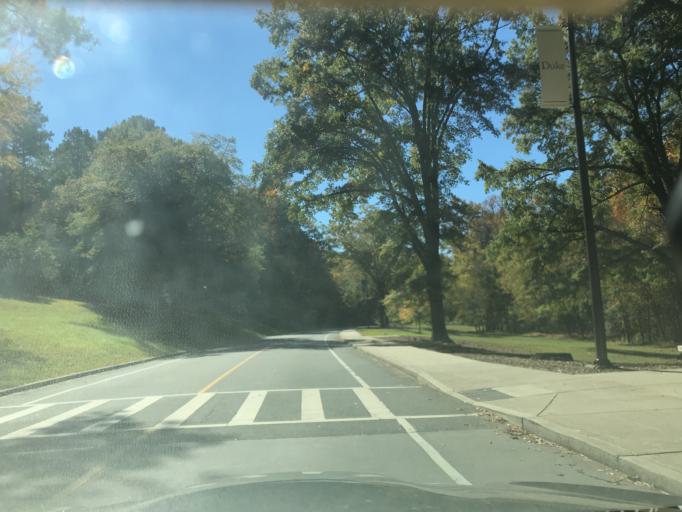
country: US
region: North Carolina
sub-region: Durham County
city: Durham
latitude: 36.0011
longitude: -78.9187
